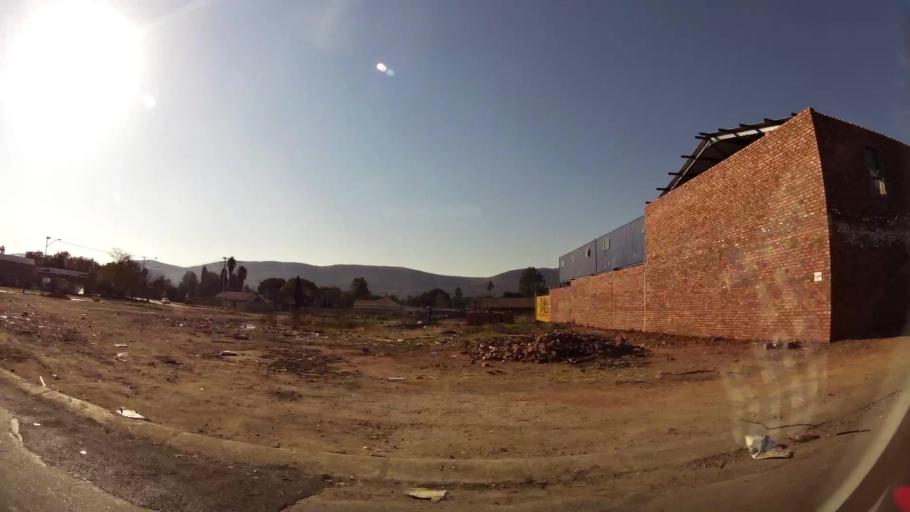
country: ZA
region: Gauteng
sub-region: City of Tshwane Metropolitan Municipality
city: Pretoria
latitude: -25.7120
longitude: 28.1560
